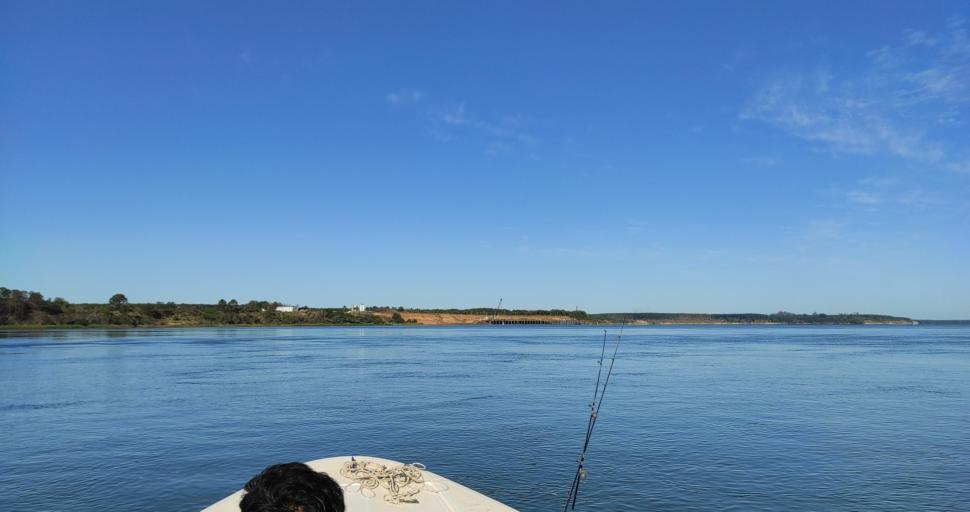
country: AR
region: Corrientes
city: Ituzaingo
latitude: -27.6053
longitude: -56.8263
